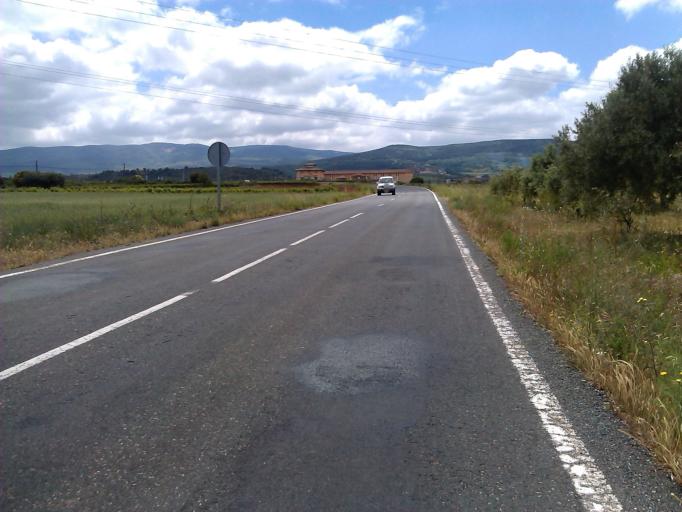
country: ES
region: La Rioja
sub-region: Provincia de La Rioja
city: Hornos de Moncalvillo
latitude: 42.4185
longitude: -2.5913
